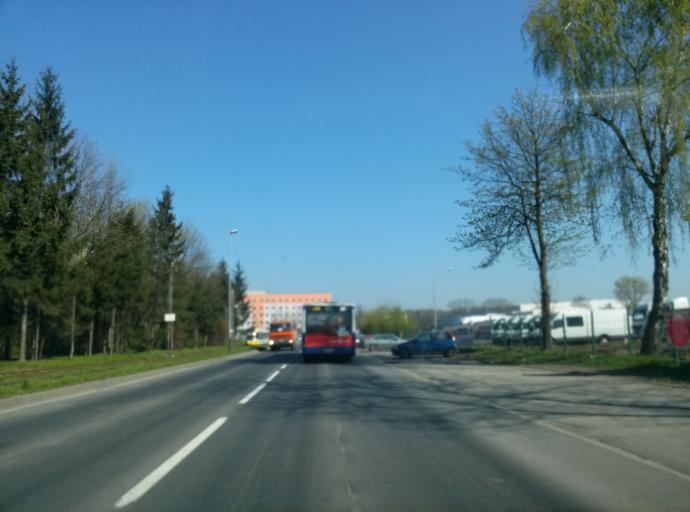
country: PL
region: Lesser Poland Voivodeship
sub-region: Powiat wielicki
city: Kokotow
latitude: 50.0856
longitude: 20.0656
